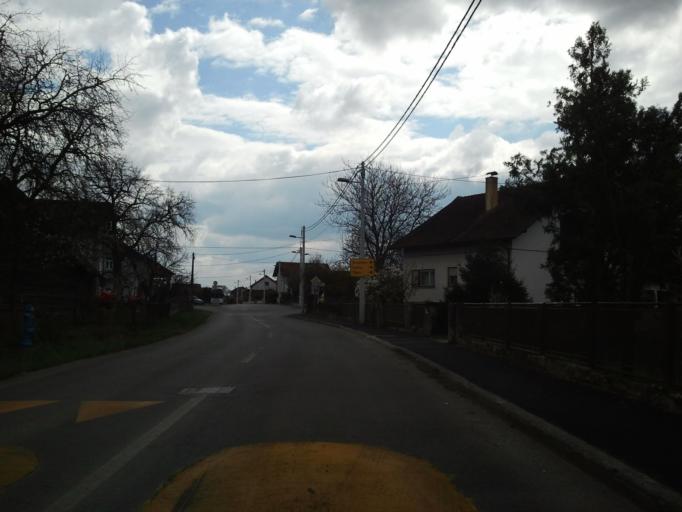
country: HR
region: Grad Zagreb
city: Strmec
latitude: 45.7165
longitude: 15.9409
